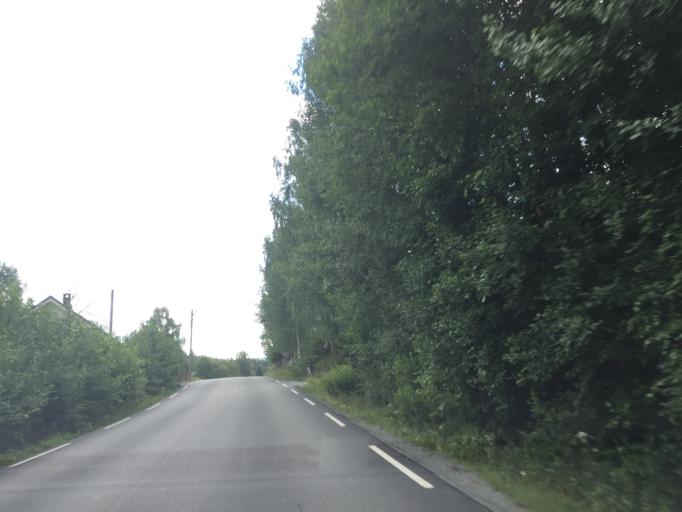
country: NO
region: Hedmark
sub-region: Kongsvinger
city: Spetalen
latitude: 60.1973
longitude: 11.9114
